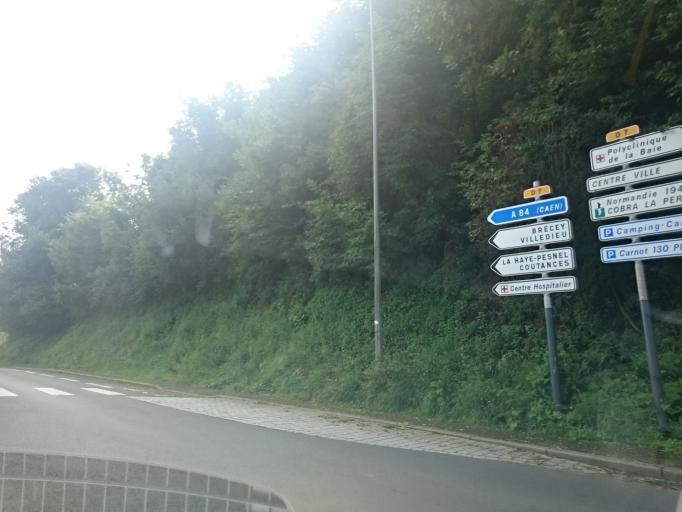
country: FR
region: Lower Normandy
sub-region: Departement de la Manche
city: Avranches
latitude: 48.6895
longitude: -1.3599
